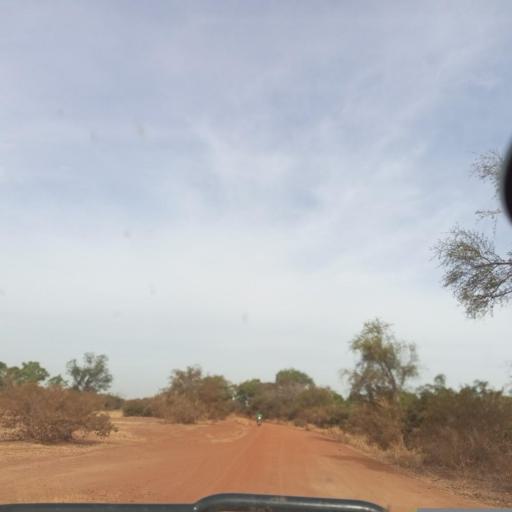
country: ML
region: Koulikoro
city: Koulikoro
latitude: 13.1049
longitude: -7.6446
